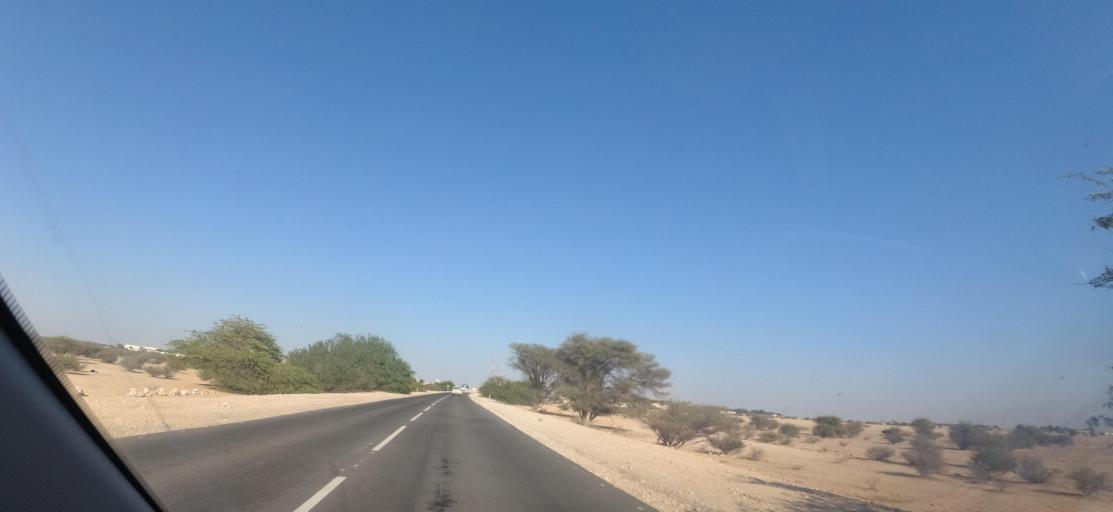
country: QA
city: Al Ghuwayriyah
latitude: 25.8225
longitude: 51.2400
